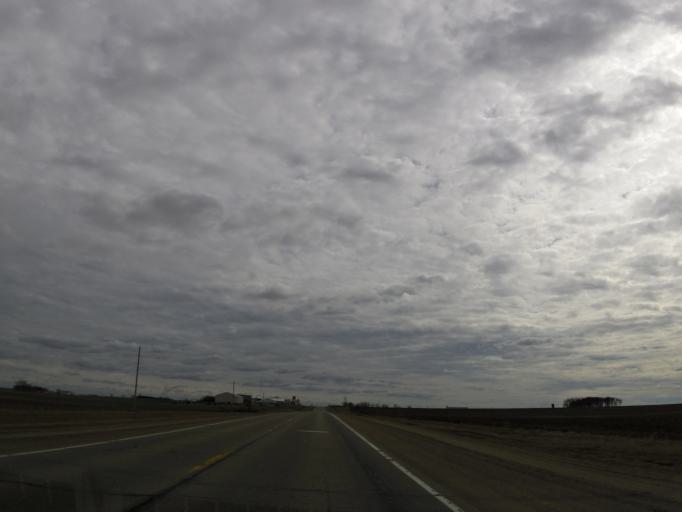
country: US
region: Iowa
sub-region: Howard County
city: Cresco
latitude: 43.3802
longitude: -92.2982
